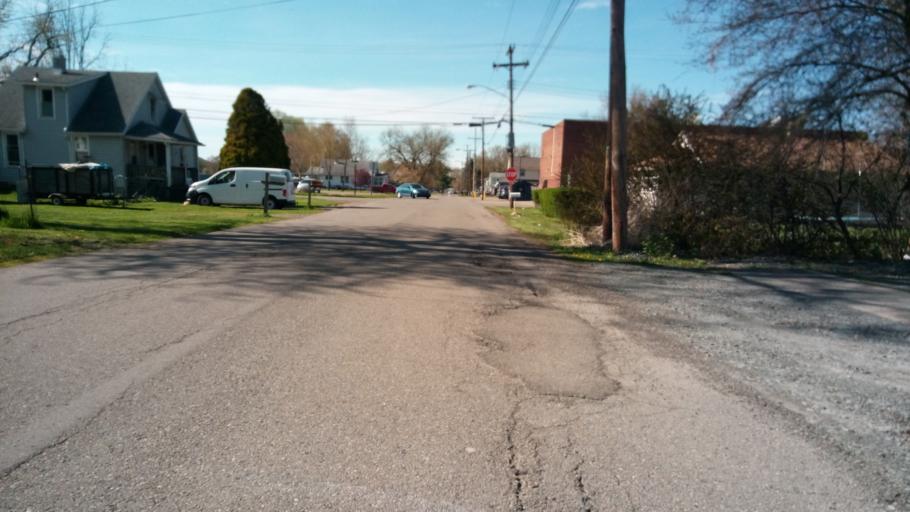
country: US
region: New York
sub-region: Chemung County
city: Southport
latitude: 42.0620
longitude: -76.7965
